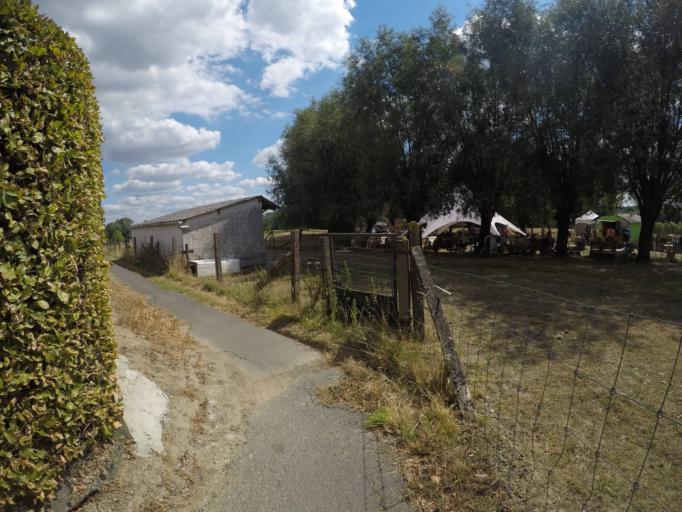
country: BE
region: Flanders
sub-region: Provincie Vlaams-Brabant
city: Ledeberg
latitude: 50.8491
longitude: 4.1112
